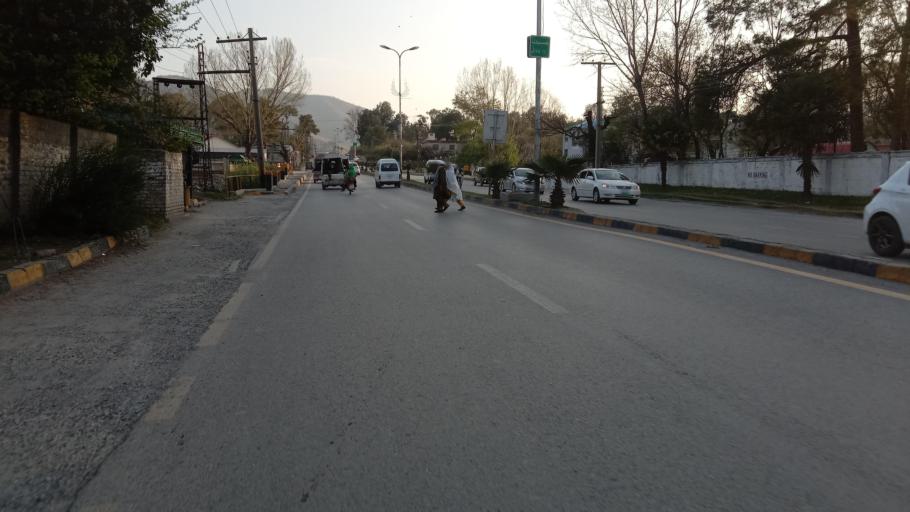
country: PK
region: Khyber Pakhtunkhwa
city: Abbottabad
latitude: 34.1611
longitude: 73.2216
